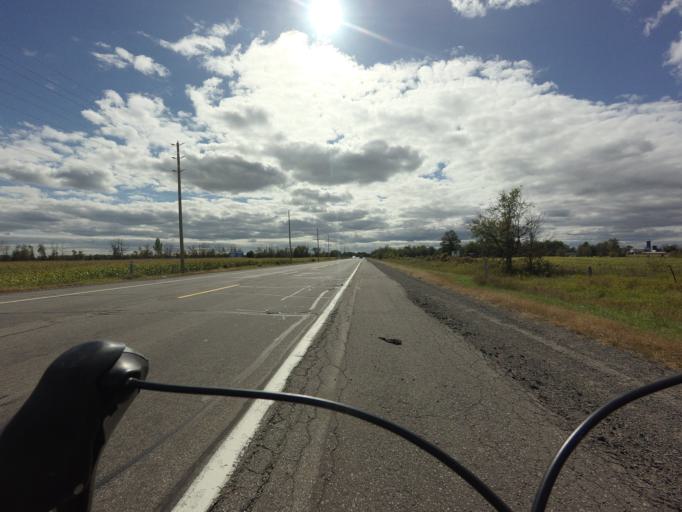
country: CA
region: Ontario
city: Bells Corners
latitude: 45.2288
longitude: -75.7166
